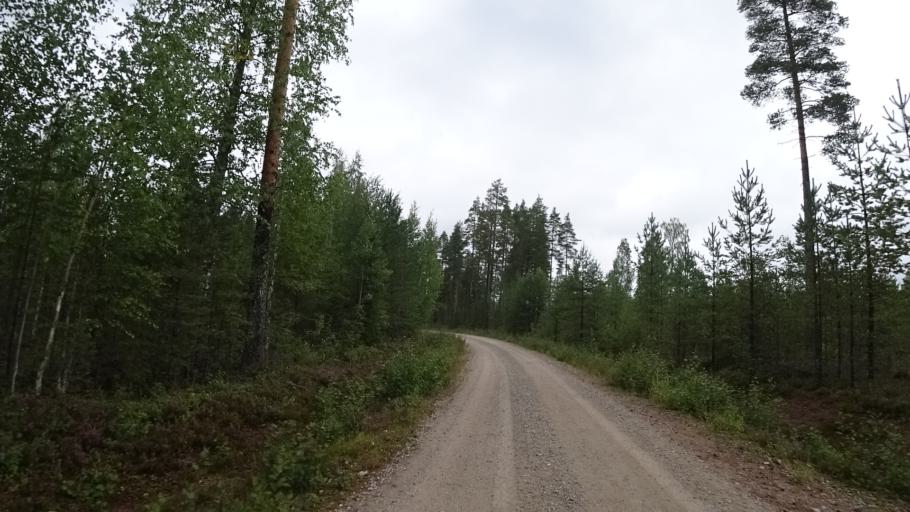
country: FI
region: North Karelia
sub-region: Pielisen Karjala
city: Lieksa
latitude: 63.5106
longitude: 30.1398
